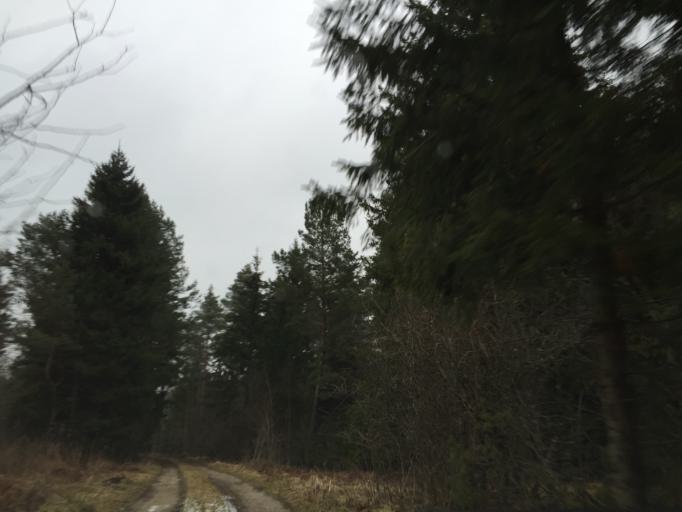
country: EE
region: Saare
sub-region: Kuressaare linn
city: Kuressaare
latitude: 58.4933
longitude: 22.3734
